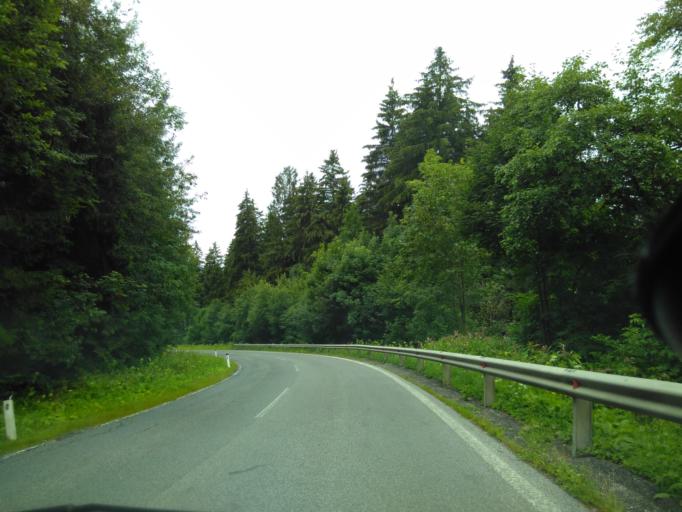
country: AT
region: Styria
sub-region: Politischer Bezirk Graz-Umgebung
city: Semriach
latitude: 47.2692
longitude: 15.4136
